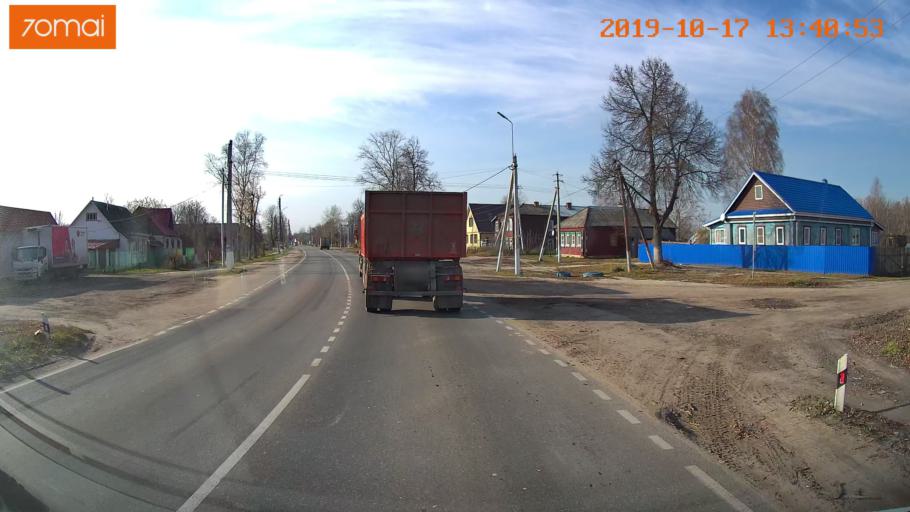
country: RU
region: Rjazan
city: Tuma
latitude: 55.1490
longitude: 40.5699
